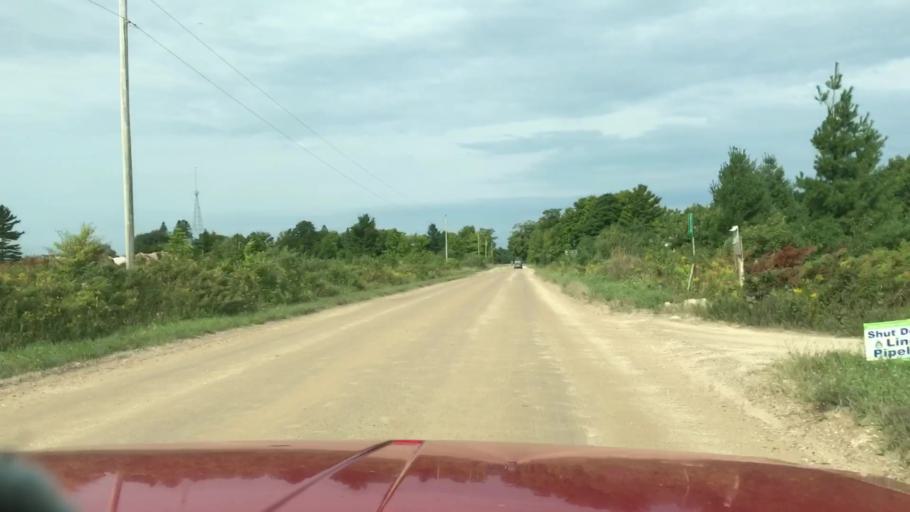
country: US
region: Michigan
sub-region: Charlevoix County
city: Charlevoix
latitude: 45.7285
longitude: -85.5181
